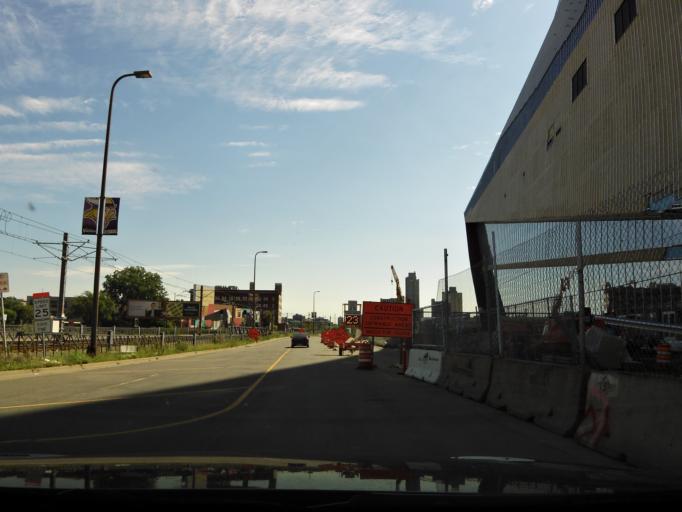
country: US
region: Minnesota
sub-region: Hennepin County
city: Minneapolis
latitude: 44.9750
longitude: -93.2573
